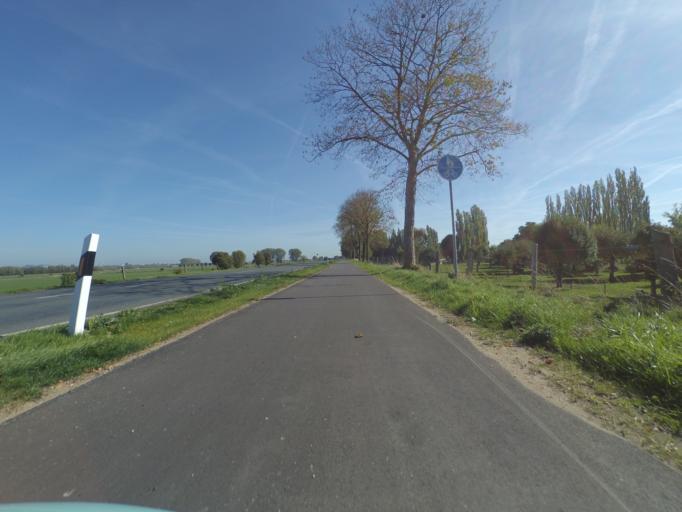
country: DE
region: North Rhine-Westphalia
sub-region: Regierungsbezirk Dusseldorf
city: Emmerich
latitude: 51.8212
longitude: 6.2294
